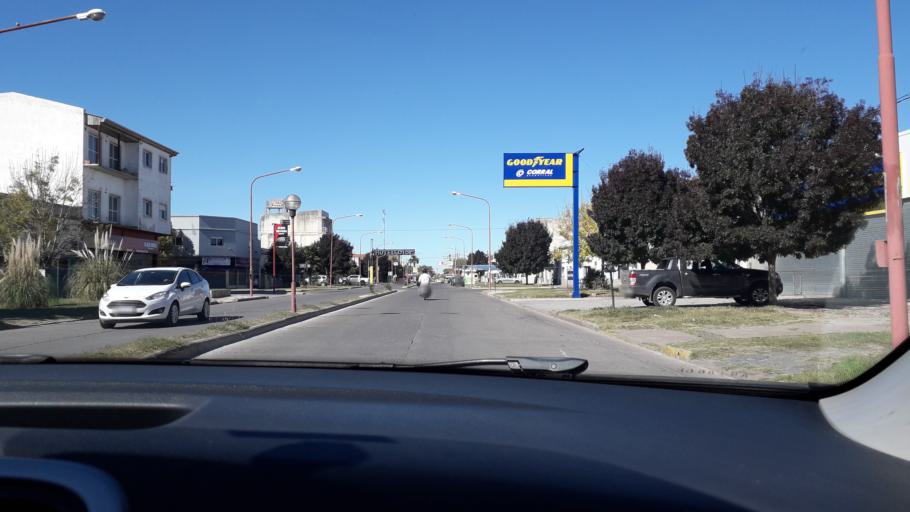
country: AR
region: Buenos Aires
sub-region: Partido de Azul
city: Azul
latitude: -36.7814
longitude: -59.8540
